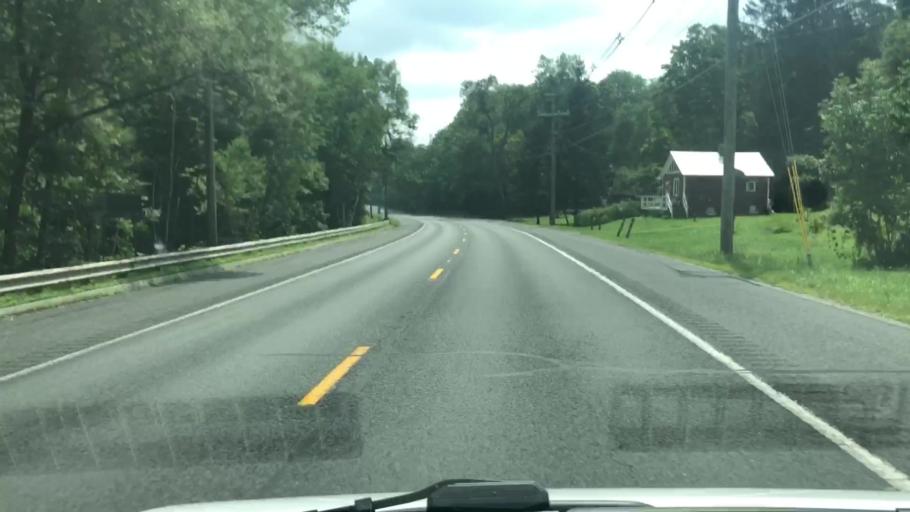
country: US
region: Massachusetts
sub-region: Berkshire County
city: Lanesborough
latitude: 42.5733
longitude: -73.2495
